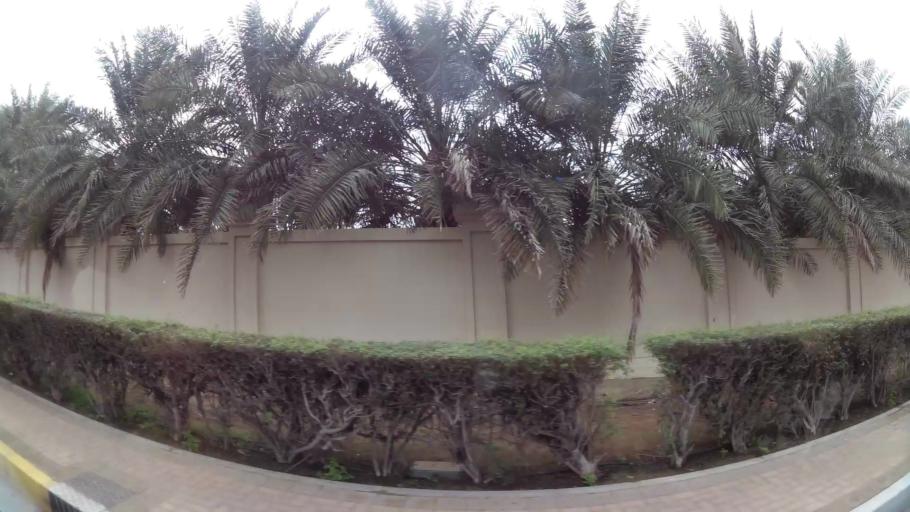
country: OM
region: Al Buraimi
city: Al Buraymi
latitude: 24.2253
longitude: 55.7725
